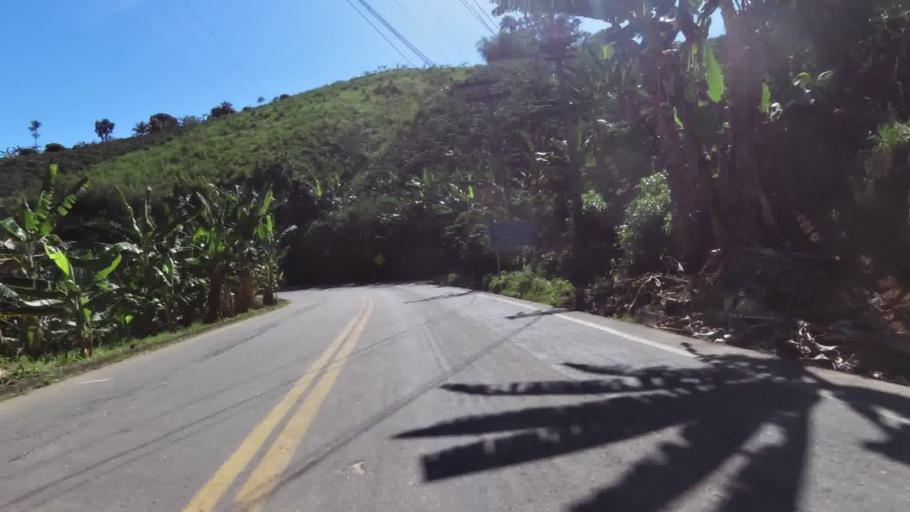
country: BR
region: Espirito Santo
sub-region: Iconha
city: Iconha
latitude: -20.7588
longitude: -40.8364
